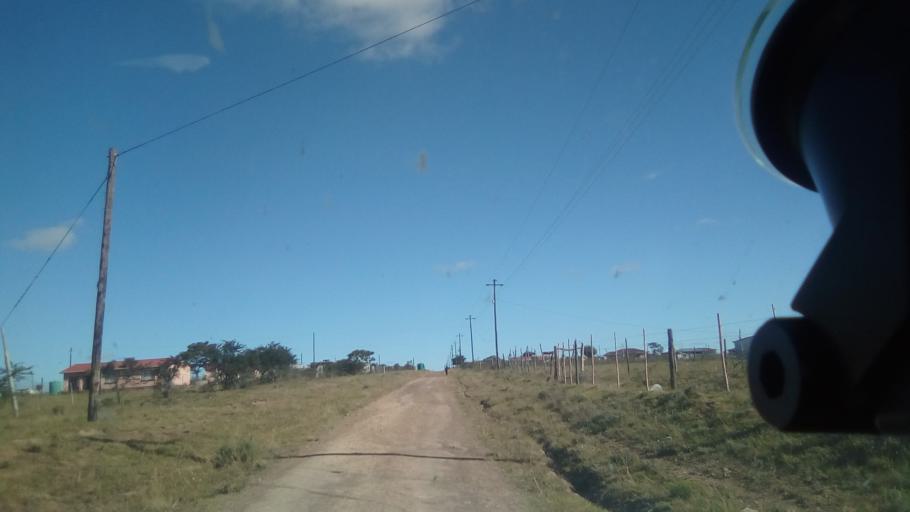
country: ZA
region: Eastern Cape
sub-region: Buffalo City Metropolitan Municipality
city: Bhisho
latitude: -32.7818
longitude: 27.3363
